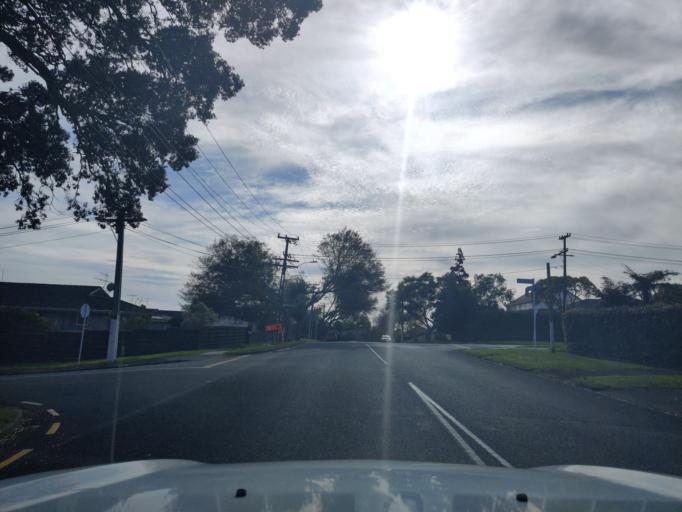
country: NZ
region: Auckland
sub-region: Auckland
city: Tamaki
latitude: -36.8965
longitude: 174.8548
